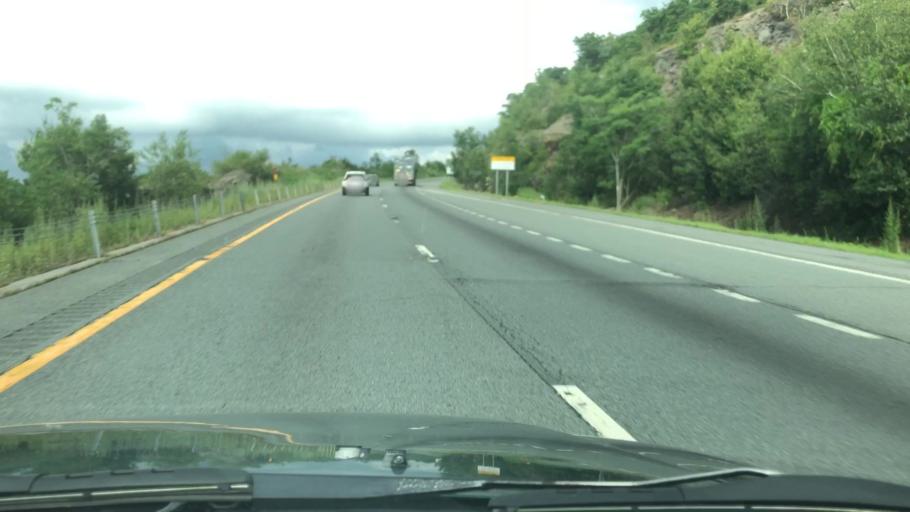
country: US
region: New York
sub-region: Orange County
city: Port Jervis
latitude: 41.3736
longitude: -74.6371
